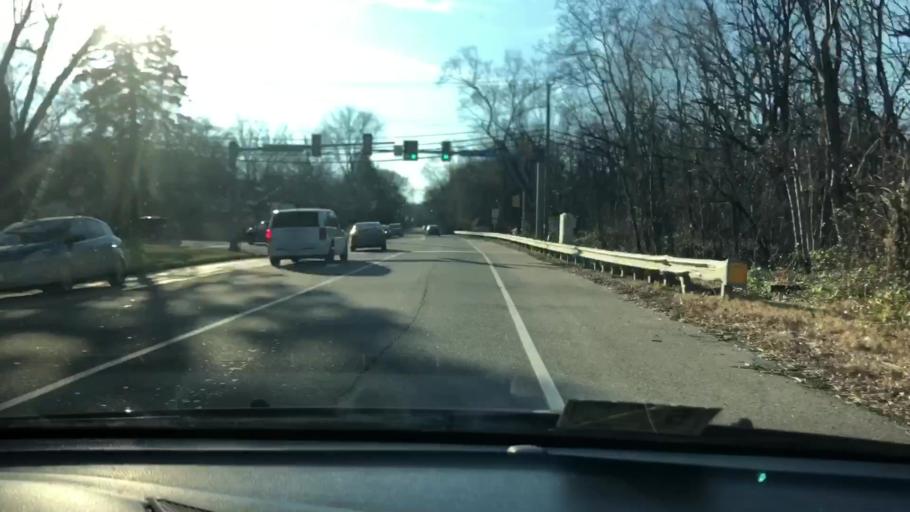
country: US
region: Virginia
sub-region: Fairfax County
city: Rose Hill
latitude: 38.7856
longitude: -77.0947
